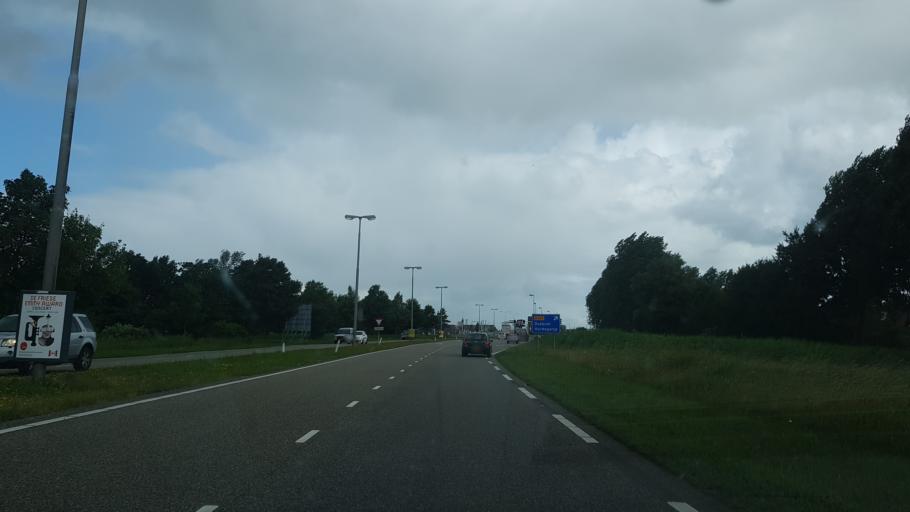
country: NL
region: Friesland
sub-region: Gemeente Leeuwarden
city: Camminghaburen
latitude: 53.2142
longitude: 5.8296
